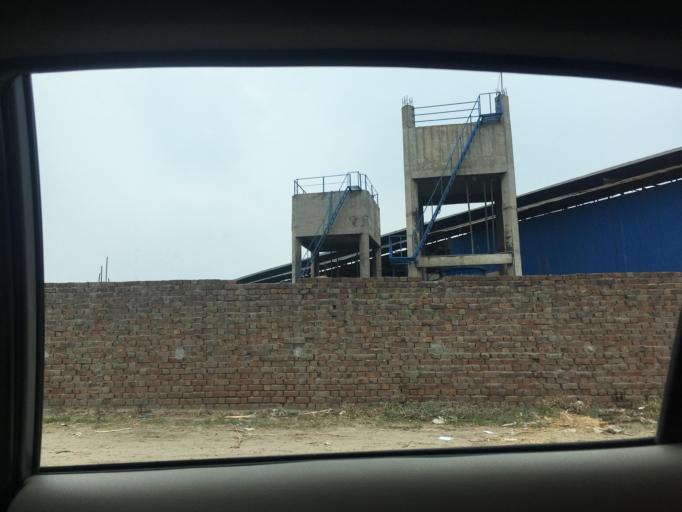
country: PK
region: Punjab
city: Lahore
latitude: 31.6089
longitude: 74.3542
